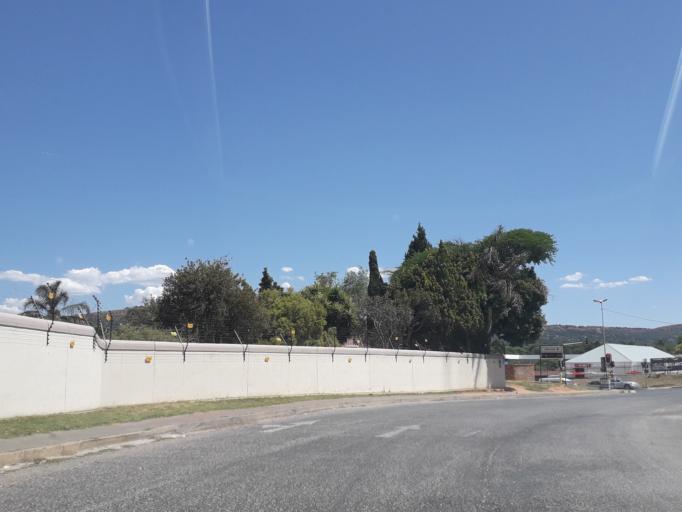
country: ZA
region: Gauteng
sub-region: City of Johannesburg Metropolitan Municipality
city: Roodepoort
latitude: -26.1189
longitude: 27.9585
